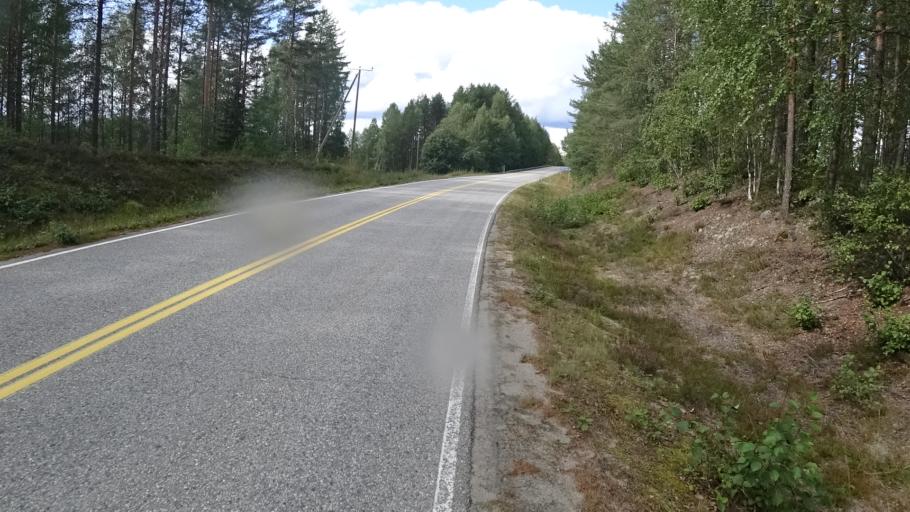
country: FI
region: North Karelia
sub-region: Joensuu
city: Ilomantsi
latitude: 62.6179
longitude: 31.2043
